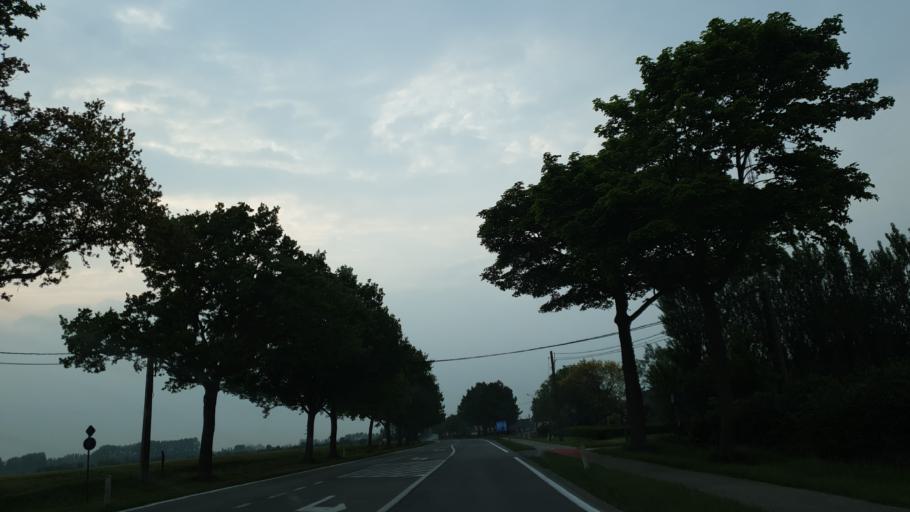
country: BE
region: Flanders
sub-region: Provincie West-Vlaanderen
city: Alveringem
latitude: 50.9417
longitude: 2.7277
